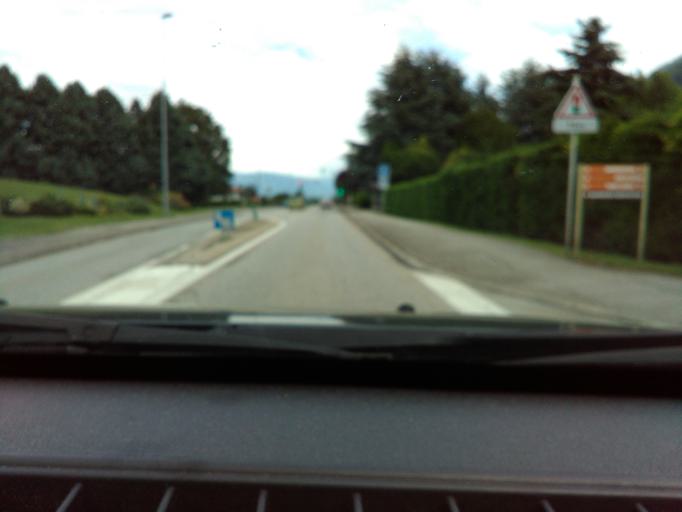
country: FR
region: Rhone-Alpes
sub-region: Departement de l'Isere
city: Le Cheylas
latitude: 45.3707
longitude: 5.9902
